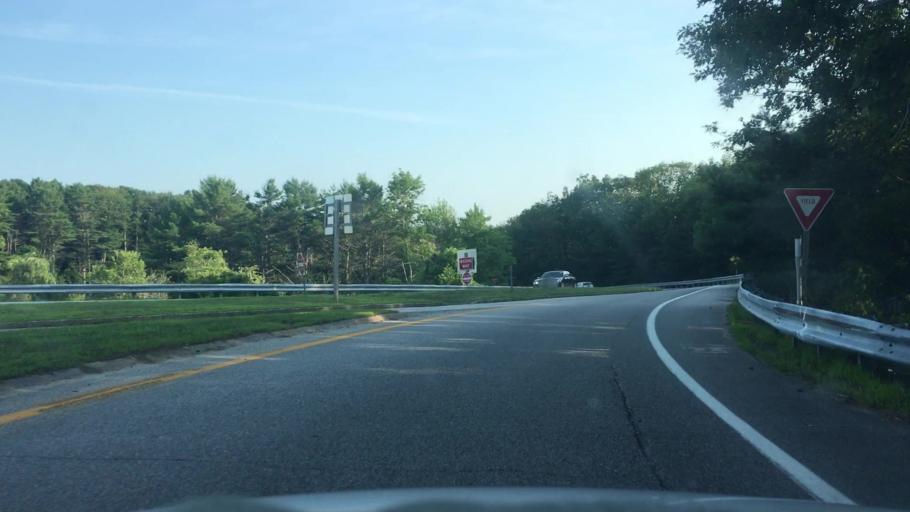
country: US
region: Maine
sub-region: Cumberland County
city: Freeport
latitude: 43.8652
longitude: -70.1093
